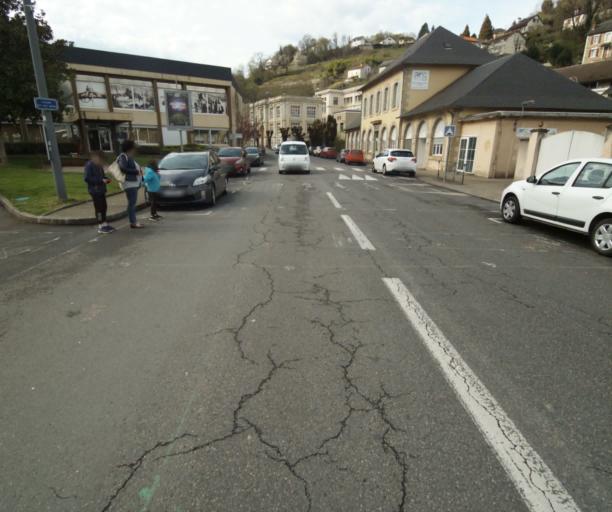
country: FR
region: Limousin
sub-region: Departement de la Correze
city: Tulle
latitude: 45.2600
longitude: 1.7519
